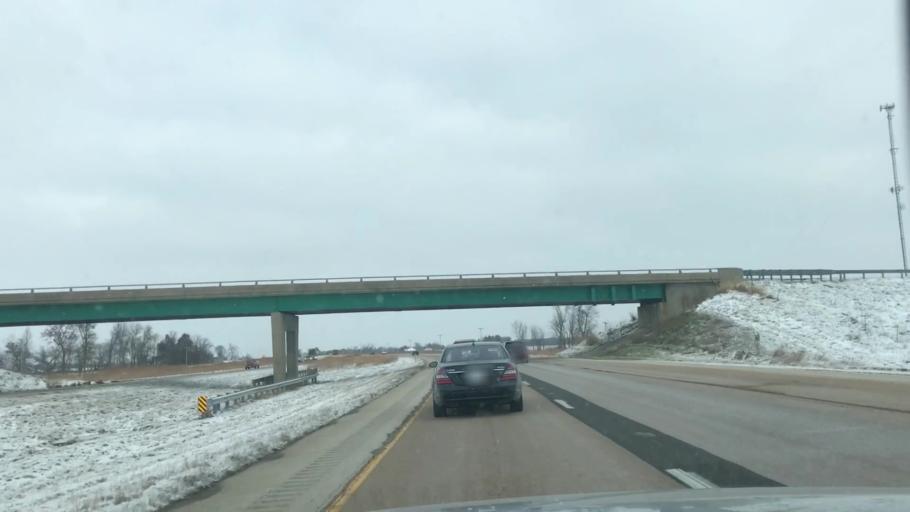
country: US
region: Illinois
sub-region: Montgomery County
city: Litchfield
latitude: 39.2334
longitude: -89.6415
